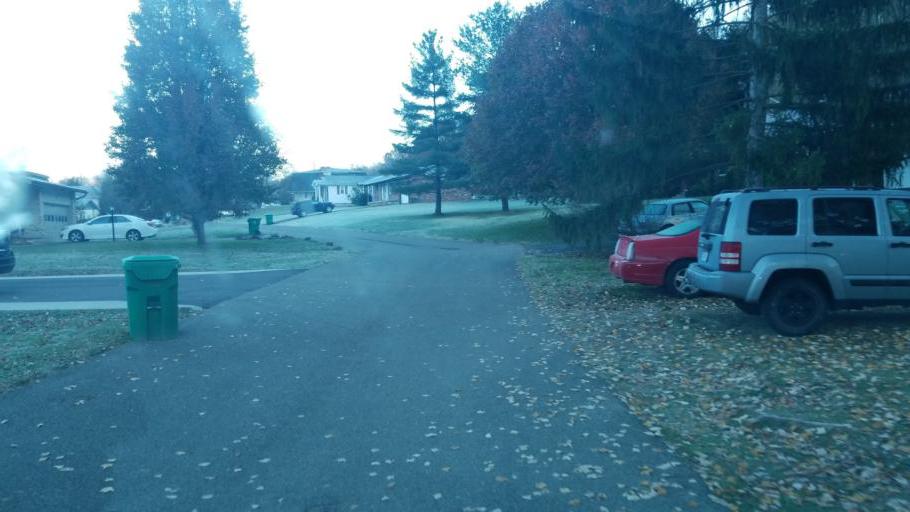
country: US
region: Kentucky
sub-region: Greenup County
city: South Shore
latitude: 38.7500
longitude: -82.9694
